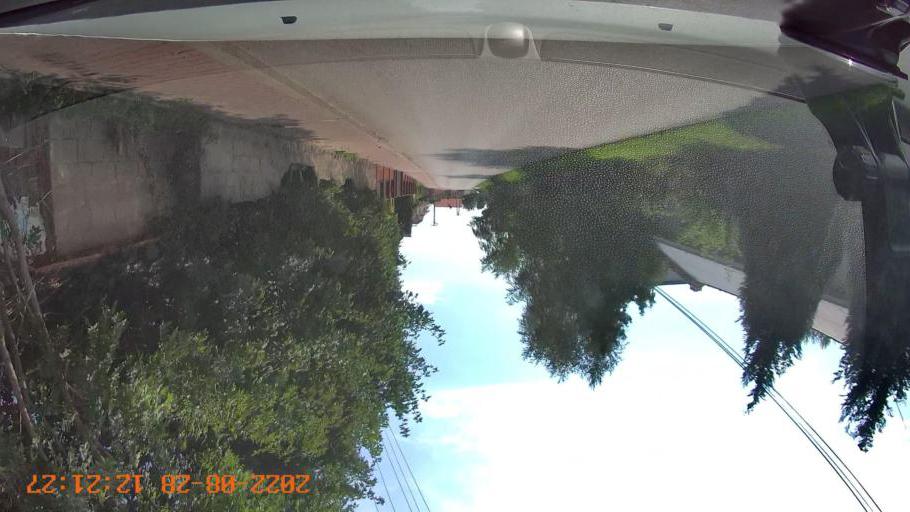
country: PL
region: Swietokrzyskie
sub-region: Powiat pinczowski
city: Zlota
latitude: 50.4235
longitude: 20.5570
